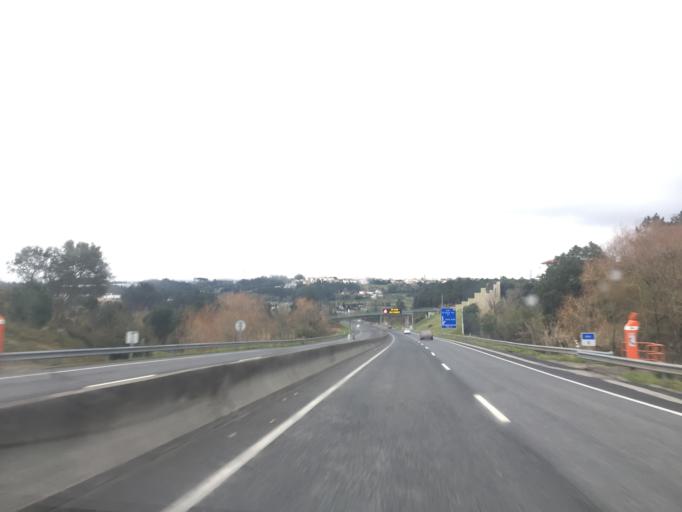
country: PT
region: Leiria
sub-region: Leiria
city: Leiria
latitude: 39.7573
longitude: -8.7754
